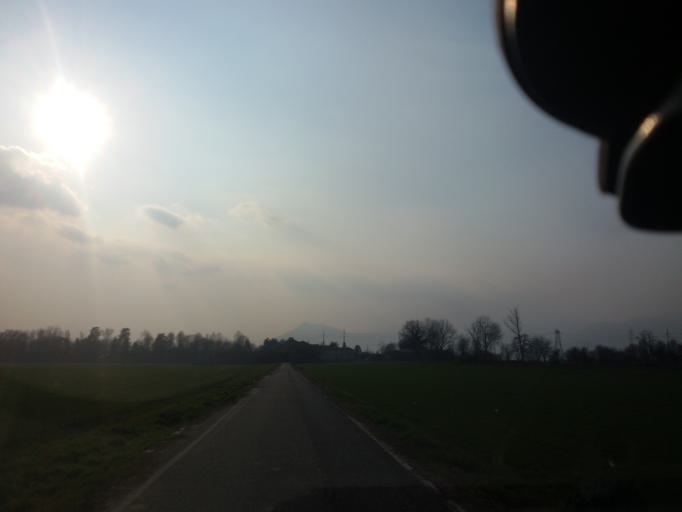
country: IT
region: Piedmont
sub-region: Provincia di Torino
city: Savonera
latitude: 45.1075
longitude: 7.6224
